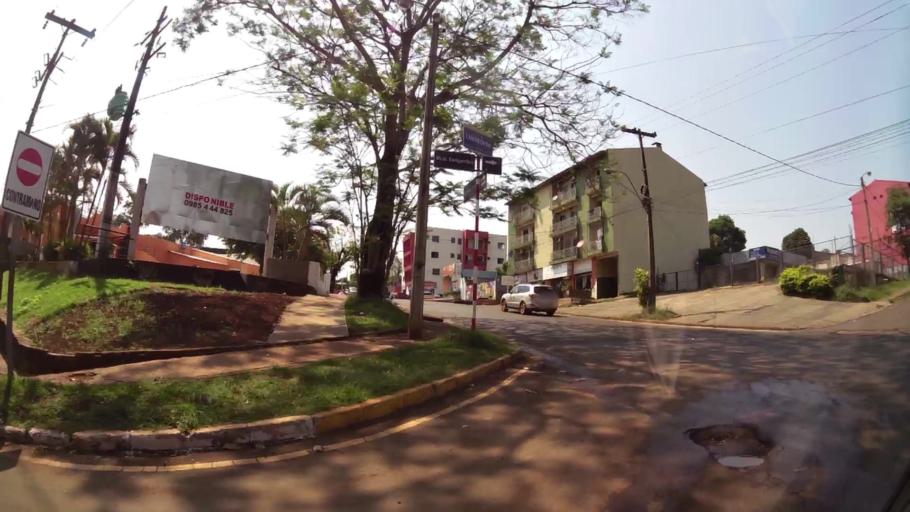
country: PY
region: Alto Parana
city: Presidente Franco
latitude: -25.5248
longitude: -54.6260
